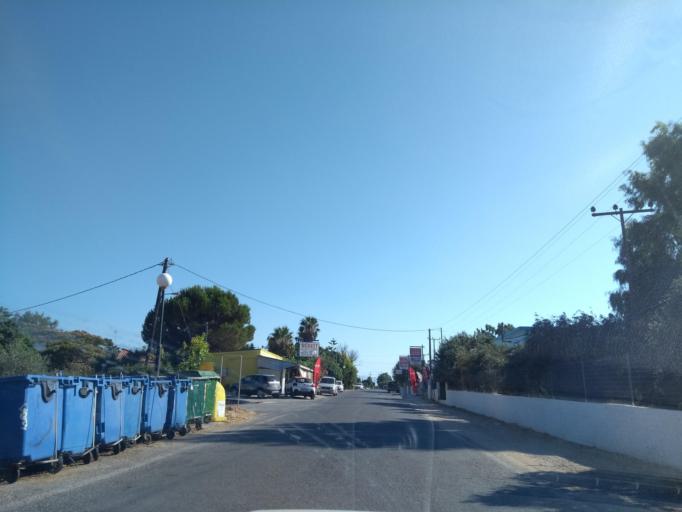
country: GR
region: Crete
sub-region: Nomos Chanias
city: Pithari
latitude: 35.5867
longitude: 24.0922
